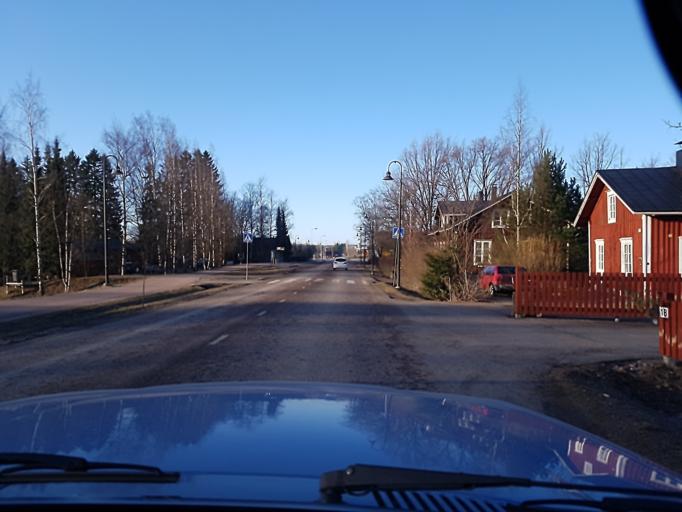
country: FI
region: Uusimaa
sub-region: Helsinki
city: Vantaa
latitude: 60.2826
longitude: 24.9836
